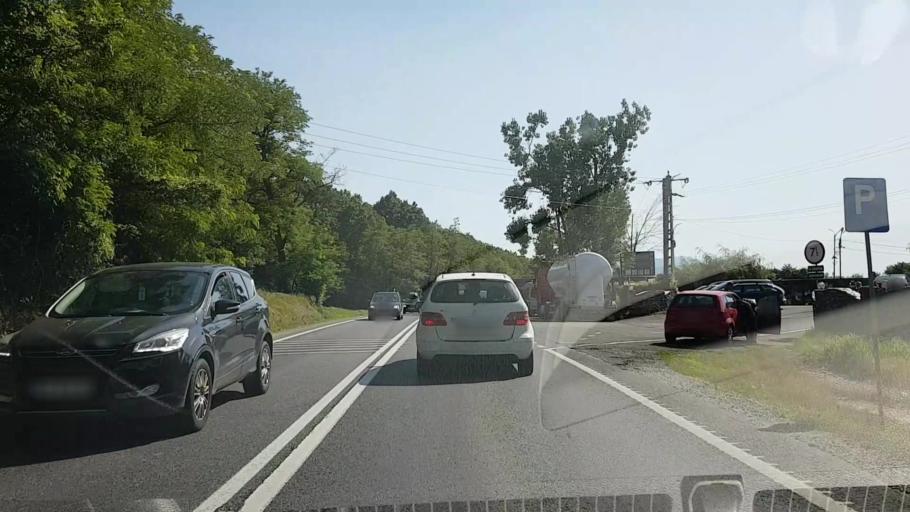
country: RO
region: Sibiu
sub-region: Comuna Avrig
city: Bradu
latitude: 45.7083
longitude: 24.2991
